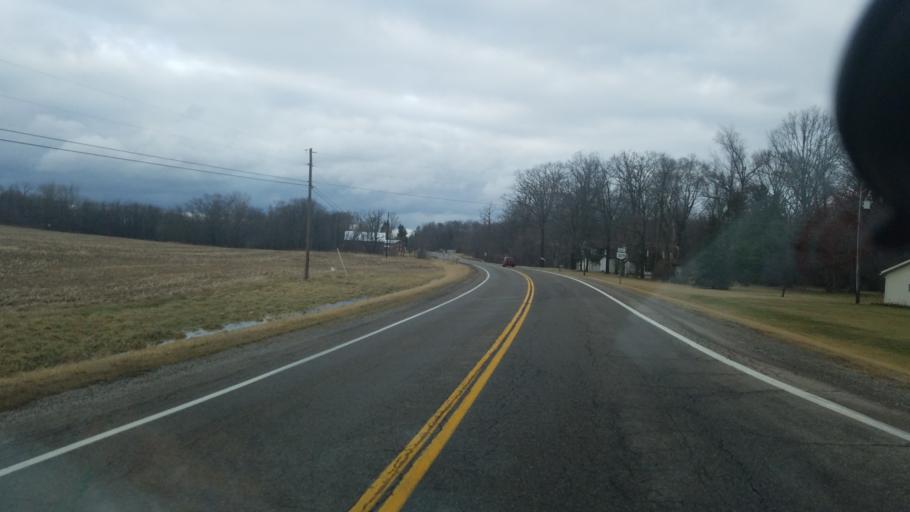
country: US
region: Ohio
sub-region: Crawford County
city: Galion
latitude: 40.6793
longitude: -82.8219
